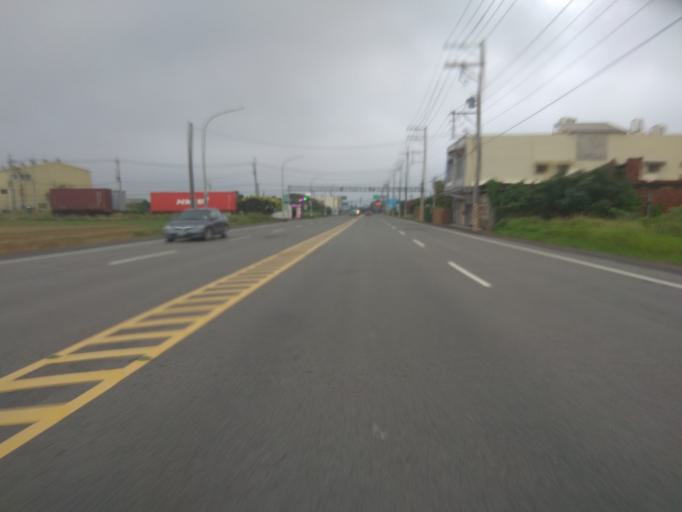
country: TW
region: Taiwan
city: Taoyuan City
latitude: 25.0326
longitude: 121.0975
